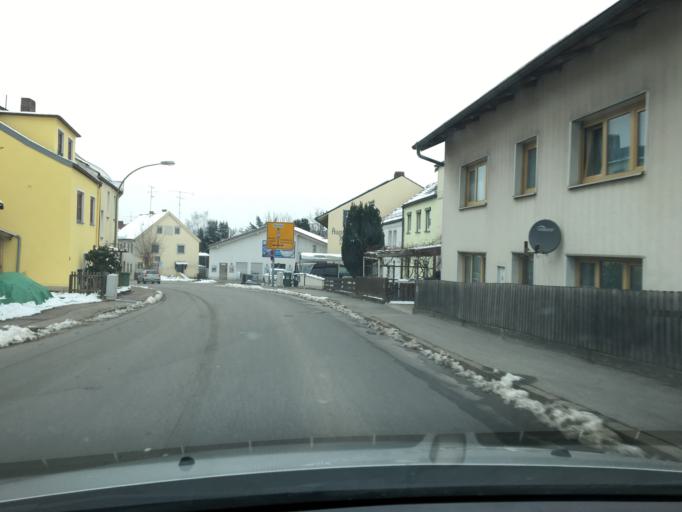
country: DE
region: Bavaria
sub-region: Lower Bavaria
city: Vilsbiburg
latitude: 48.4467
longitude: 12.3604
